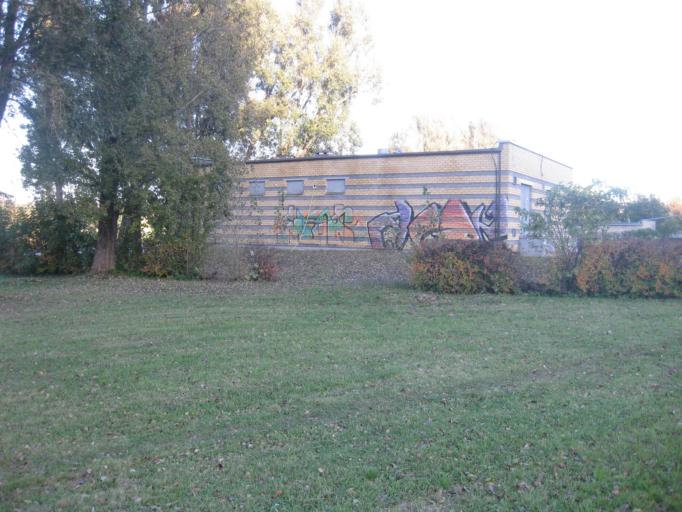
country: LT
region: Kauno apskritis
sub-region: Kaunas
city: Aleksotas
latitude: 54.8909
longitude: 23.8980
